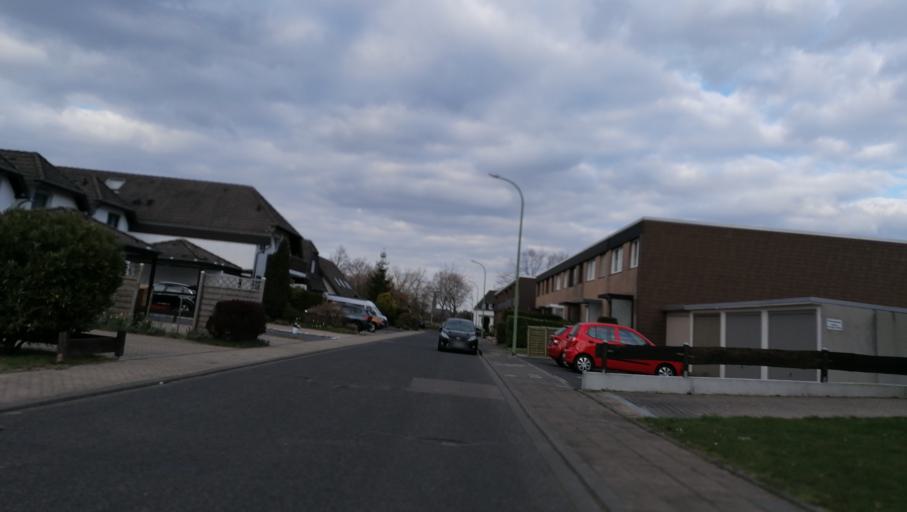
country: DE
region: North Rhine-Westphalia
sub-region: Regierungsbezirk Koln
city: Dueren
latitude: 50.7876
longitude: 6.4347
